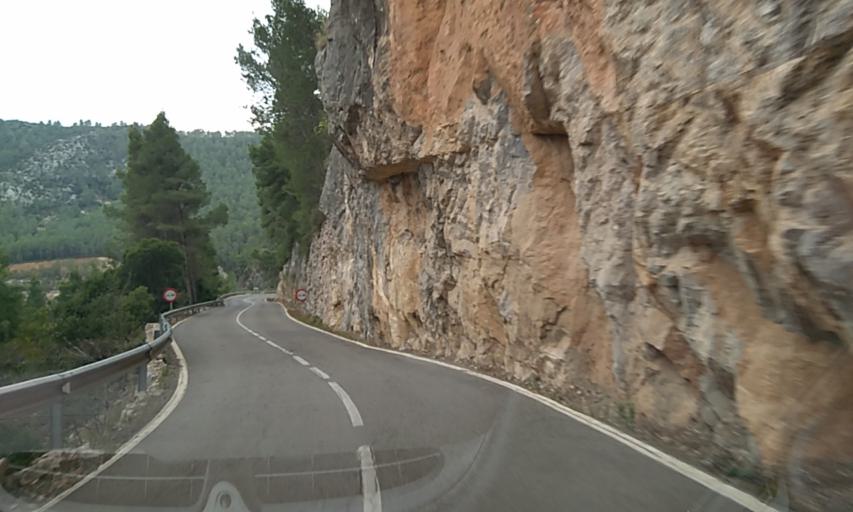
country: ES
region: Valencia
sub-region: Provincia de Castello
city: Montanejos
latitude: 40.0788
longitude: -0.5391
